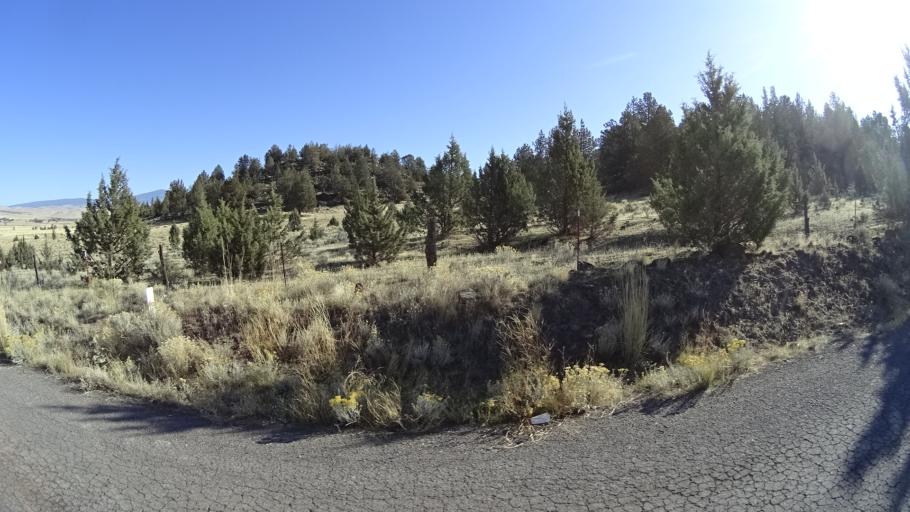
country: US
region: California
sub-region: Siskiyou County
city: Montague
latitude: 41.6995
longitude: -122.4377
